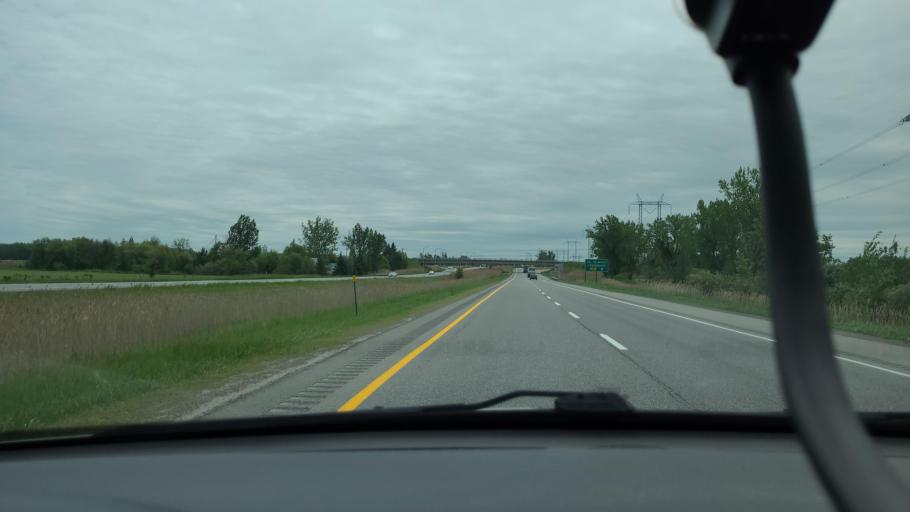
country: CA
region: Quebec
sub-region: Lanaudiere
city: Mascouche
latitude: 45.7934
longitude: -73.5824
